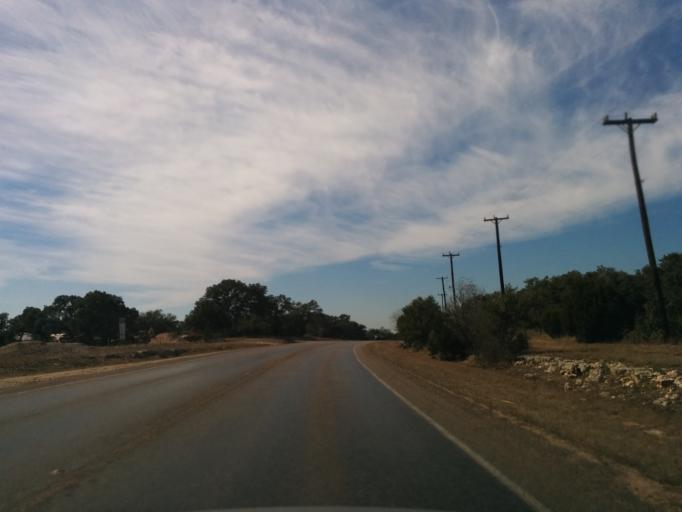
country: US
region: Texas
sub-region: Bexar County
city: Fair Oaks Ranch
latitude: 29.7571
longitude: -98.6171
